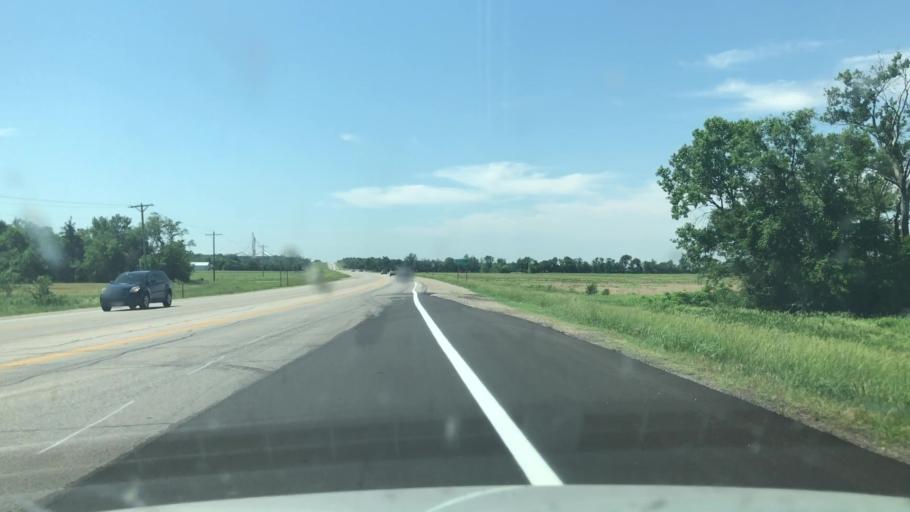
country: US
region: Kansas
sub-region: Butler County
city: Douglass
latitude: 37.3886
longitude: -97.0069
